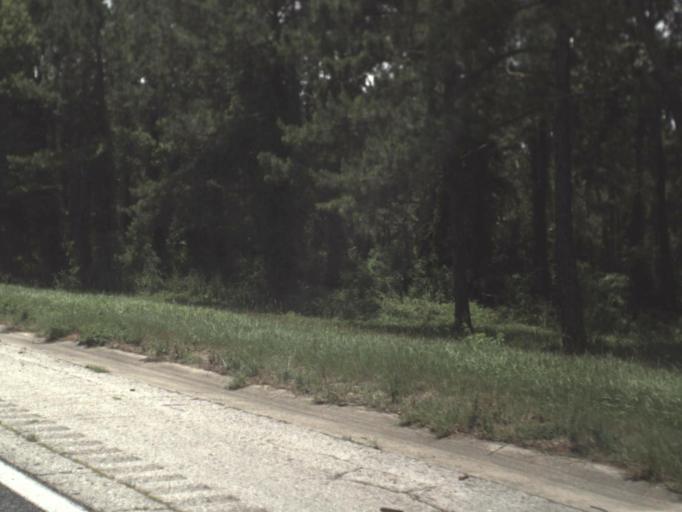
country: US
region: Florida
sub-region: Alachua County
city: Gainesville
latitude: 29.6163
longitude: -82.3856
